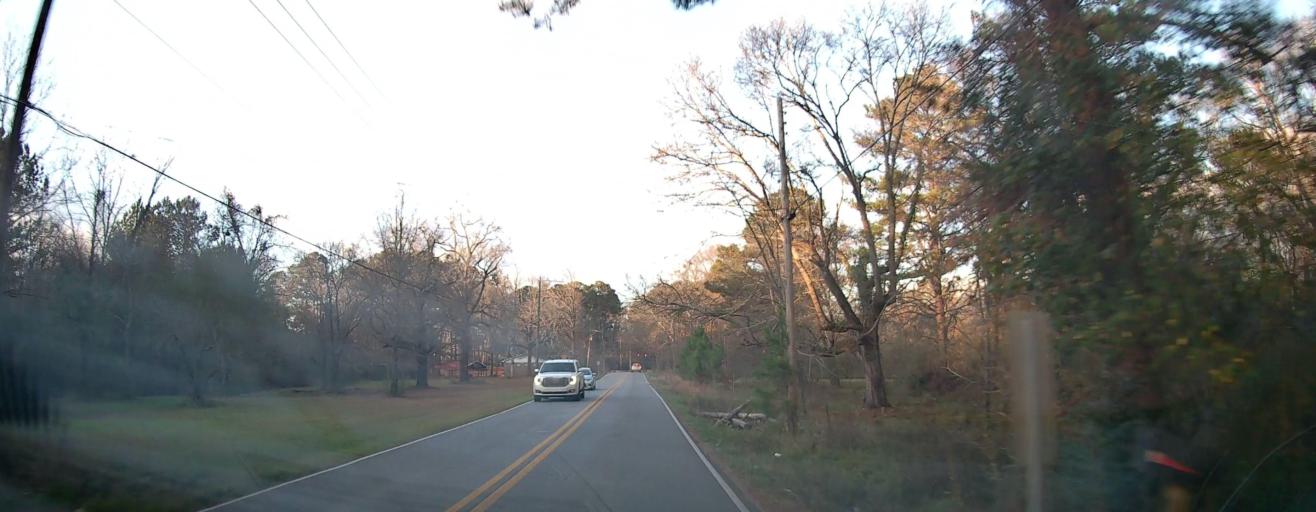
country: US
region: Alabama
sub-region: Etowah County
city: Gadsden
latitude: 33.9822
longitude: -85.9845
